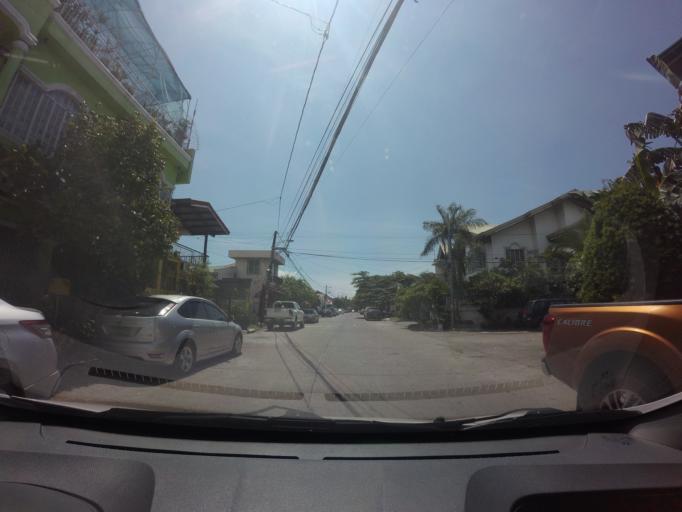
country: PH
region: Calabarzon
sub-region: Province of Rizal
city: Las Pinas
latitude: 14.4387
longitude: 120.9766
